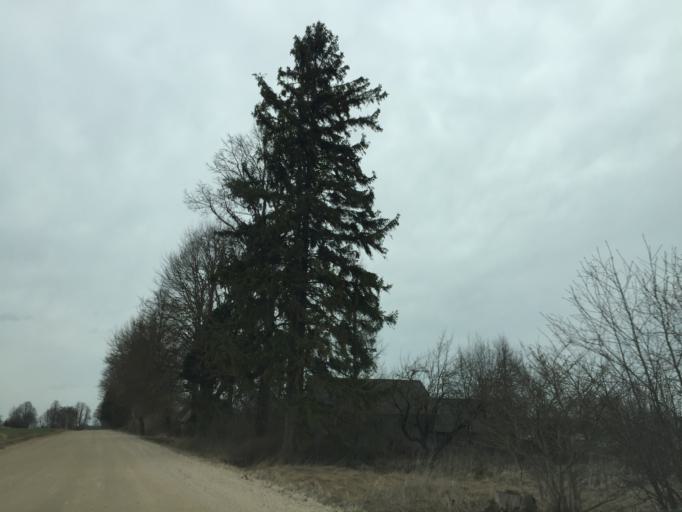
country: LV
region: Livani
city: Livani
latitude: 56.2921
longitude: 26.1753
